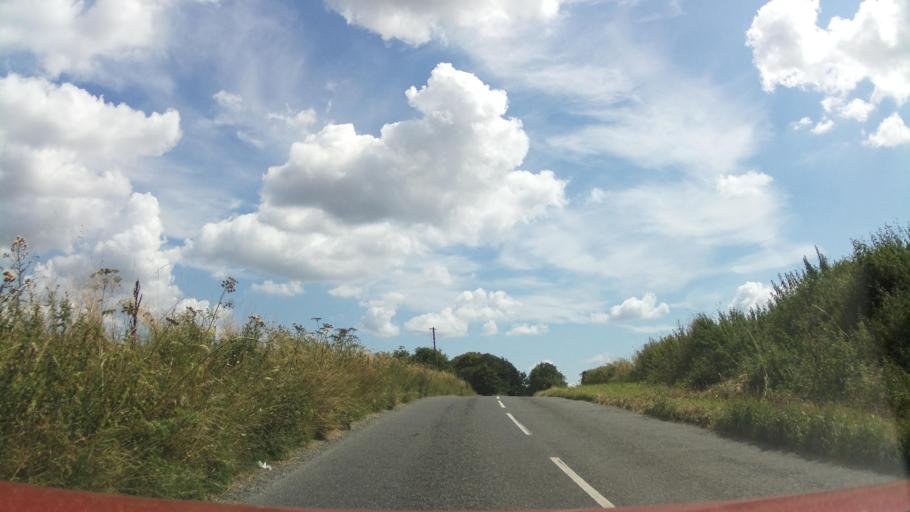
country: GB
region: England
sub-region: Borough of Swindon
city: Bishopstone
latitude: 51.5601
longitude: -1.6115
